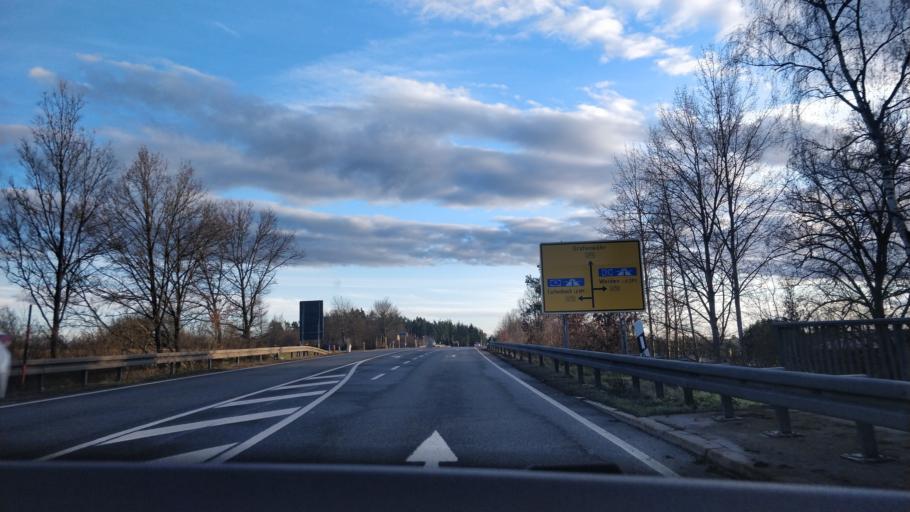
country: DE
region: Bavaria
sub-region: Upper Palatinate
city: Pressath
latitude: 49.7636
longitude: 11.9238
